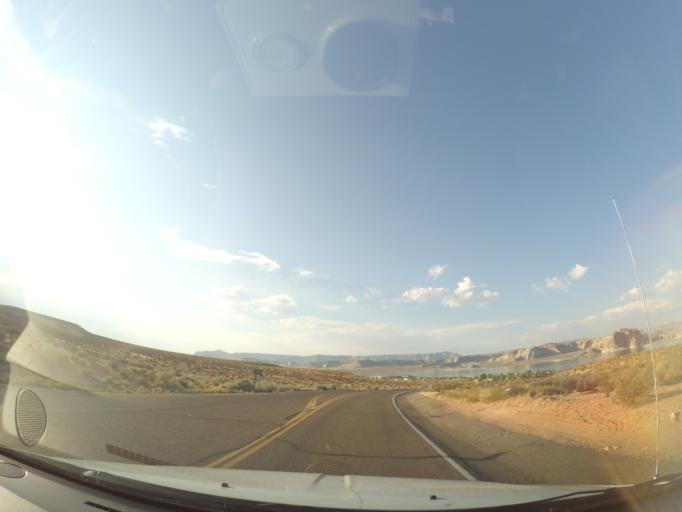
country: US
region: Arizona
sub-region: Coconino County
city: Page
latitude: 36.9943
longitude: -111.5032
